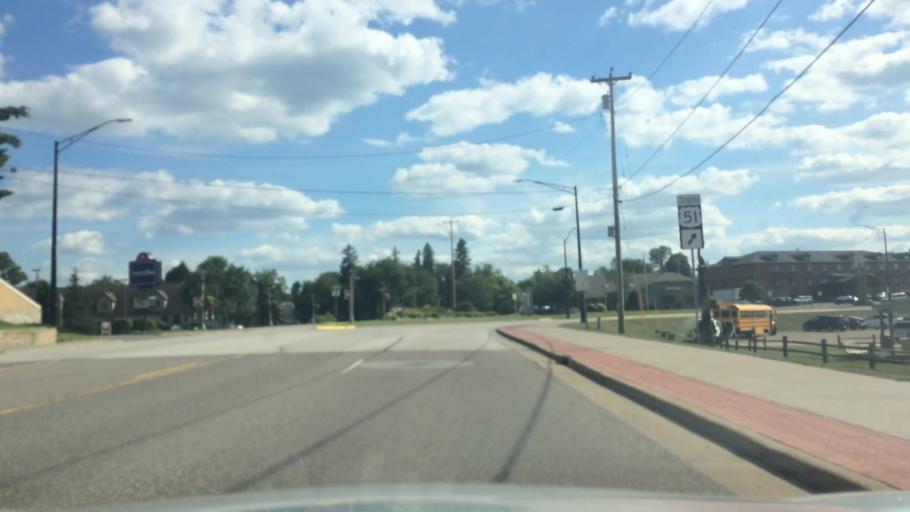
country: US
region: Wisconsin
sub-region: Vilas County
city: Lac du Flambeau
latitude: 45.8733
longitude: -89.7072
